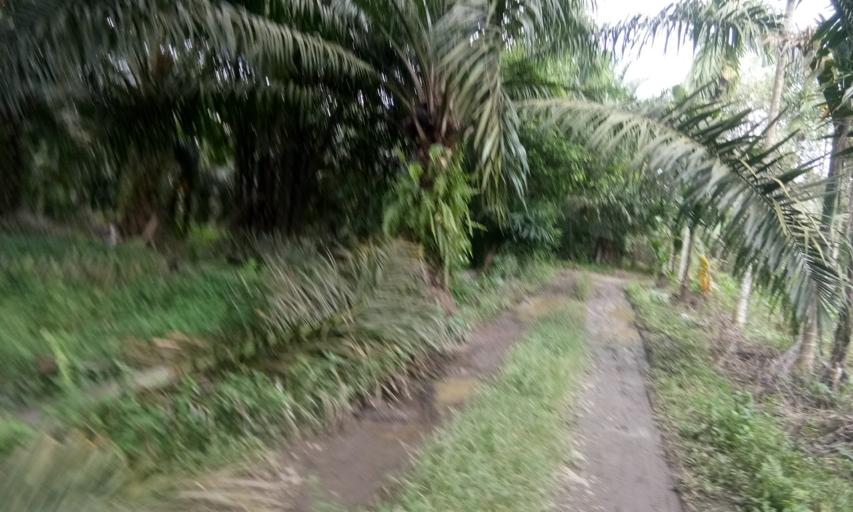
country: ID
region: North Sumatra
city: Deli Tua
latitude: 3.4650
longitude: 98.6101
